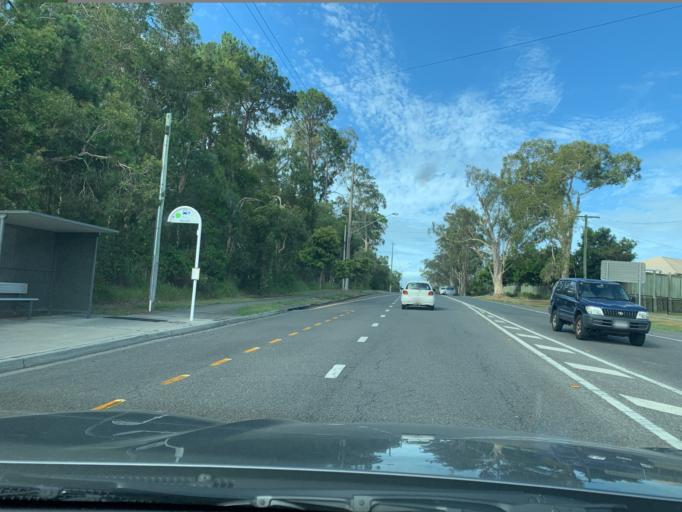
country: AU
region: Queensland
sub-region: Brisbane
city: Wynnum West
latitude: -27.4738
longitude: 153.1460
